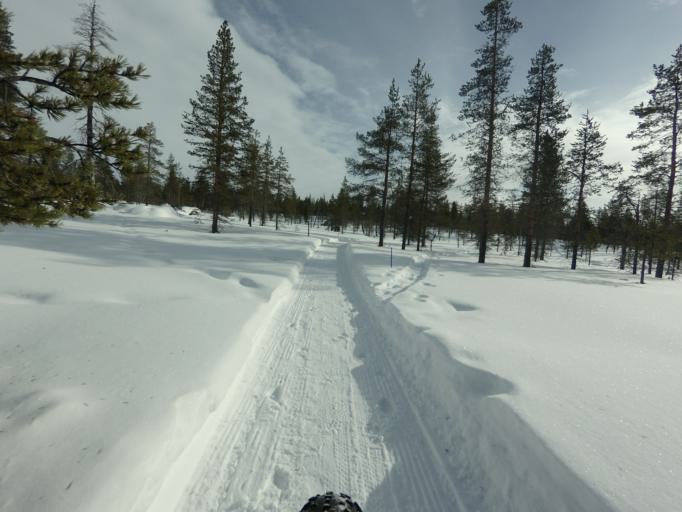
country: FI
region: Lapland
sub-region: Pohjois-Lappi
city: Ivalo
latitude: 68.3453
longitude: 27.4295
